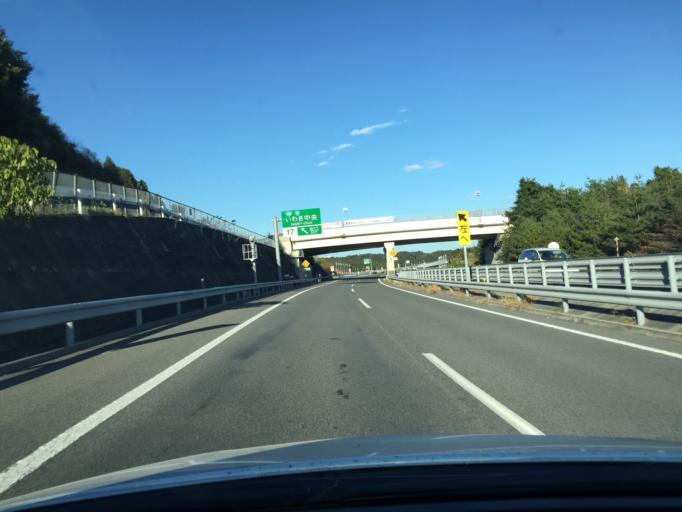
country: JP
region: Fukushima
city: Iwaki
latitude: 37.0635
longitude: 140.8336
